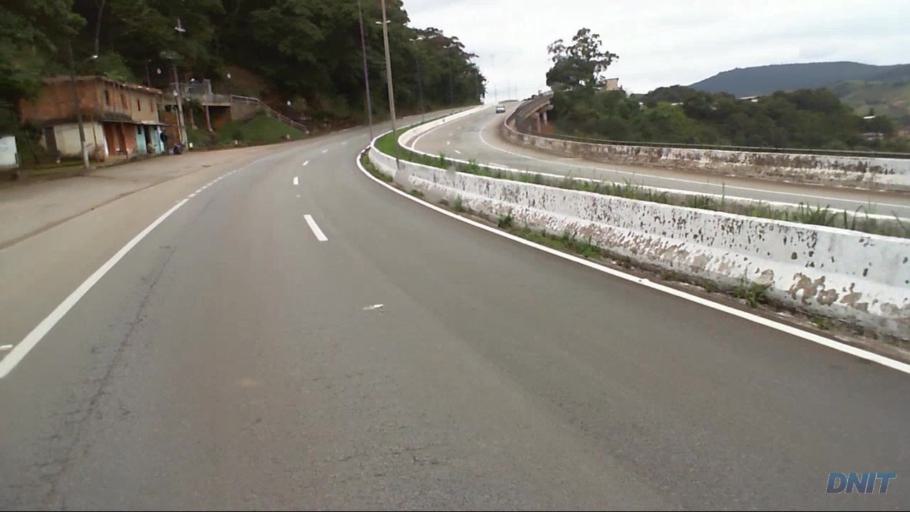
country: BR
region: Minas Gerais
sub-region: Nova Era
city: Nova Era
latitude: -19.7616
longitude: -43.0425
